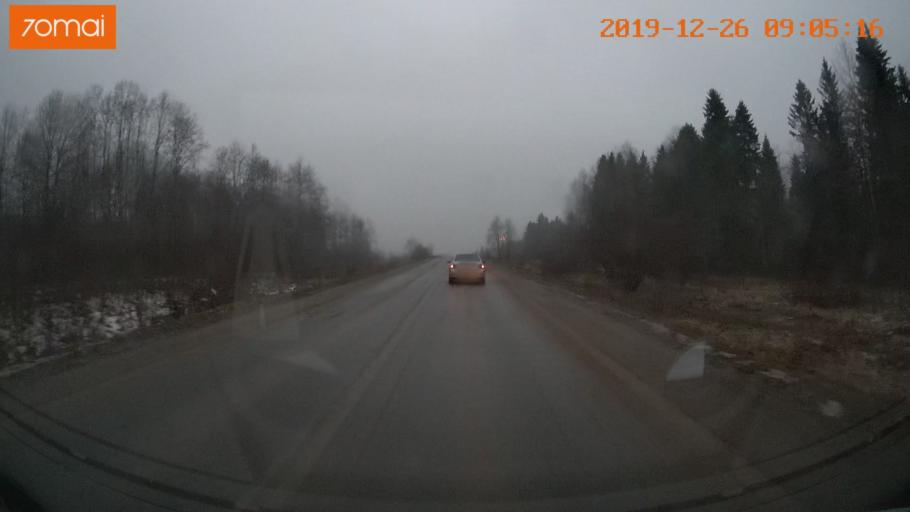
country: RU
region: Vologda
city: Gryazovets
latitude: 58.8238
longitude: 40.2588
